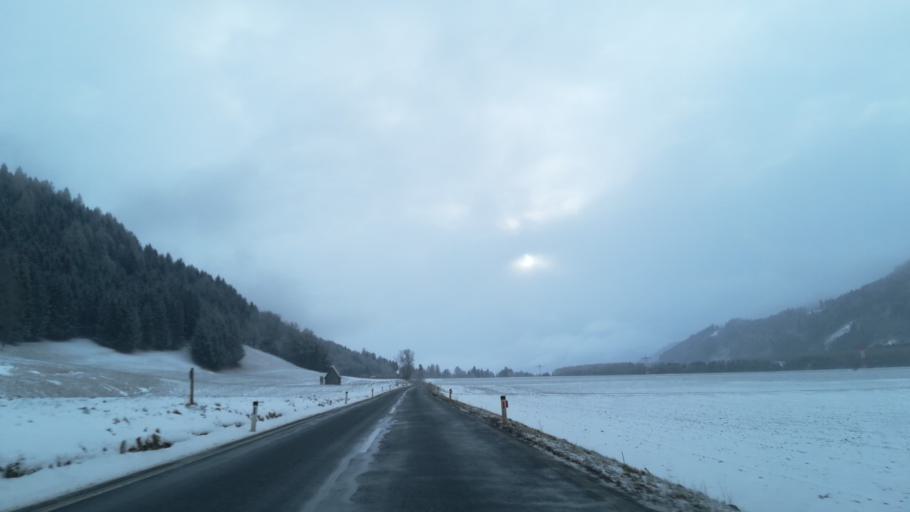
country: AT
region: Styria
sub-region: Politischer Bezirk Murtal
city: Poels
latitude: 47.2147
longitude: 14.6178
